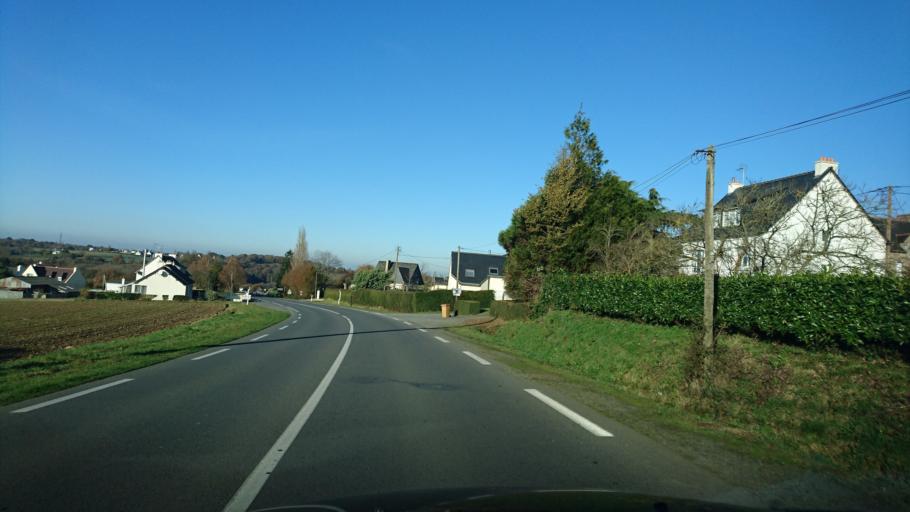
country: FR
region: Brittany
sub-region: Departement des Cotes-d'Armor
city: Pledran
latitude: 48.4557
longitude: -2.7534
